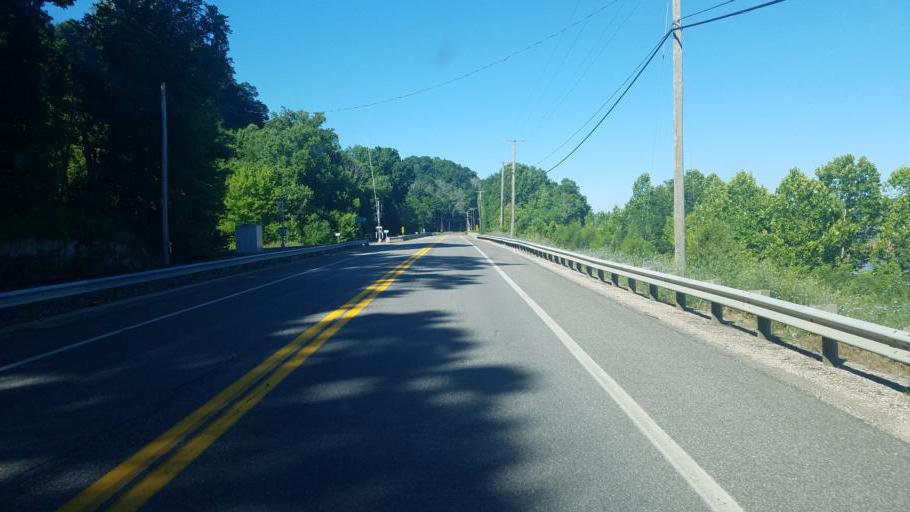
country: US
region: West Virginia
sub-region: Mason County
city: Point Pleasant
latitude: 38.8202
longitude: -82.1606
